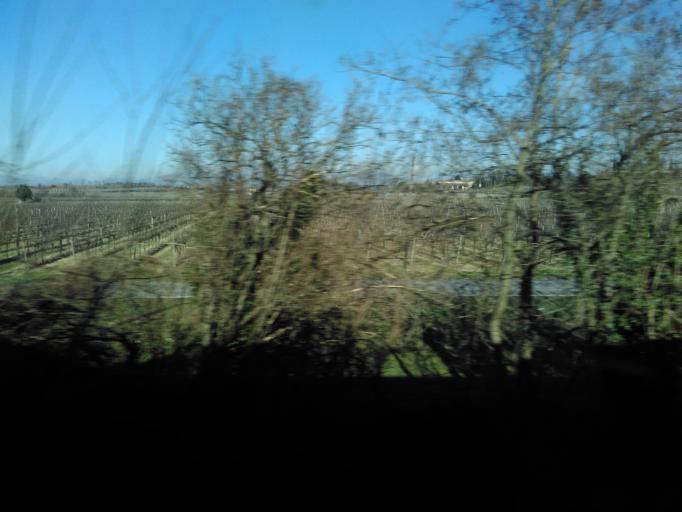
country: IT
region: Veneto
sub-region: Provincia di Verona
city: San Giorgio in Salici
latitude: 45.4229
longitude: 10.8053
